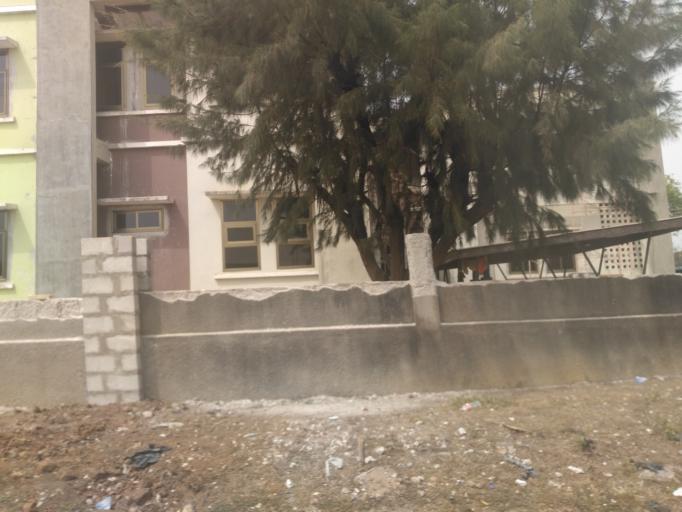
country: GH
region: Ashanti
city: Kumasi
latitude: 6.7030
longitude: -1.6133
